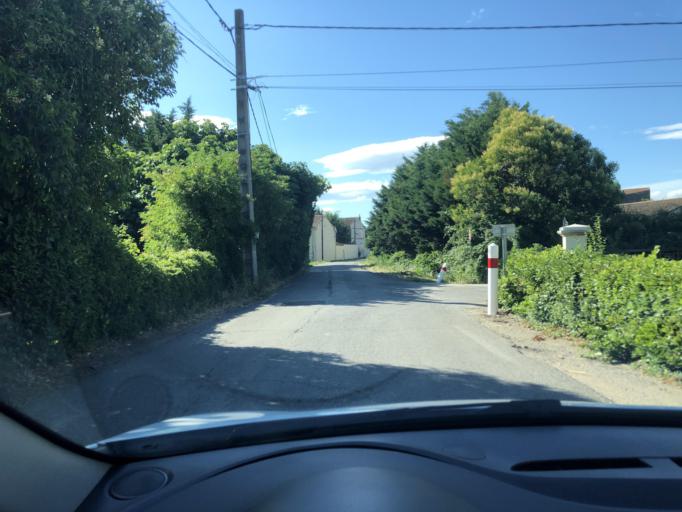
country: FR
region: Provence-Alpes-Cote d'Azur
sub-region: Departement des Bouches-du-Rhone
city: Chateaurenard
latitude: 43.8930
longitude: 4.8450
